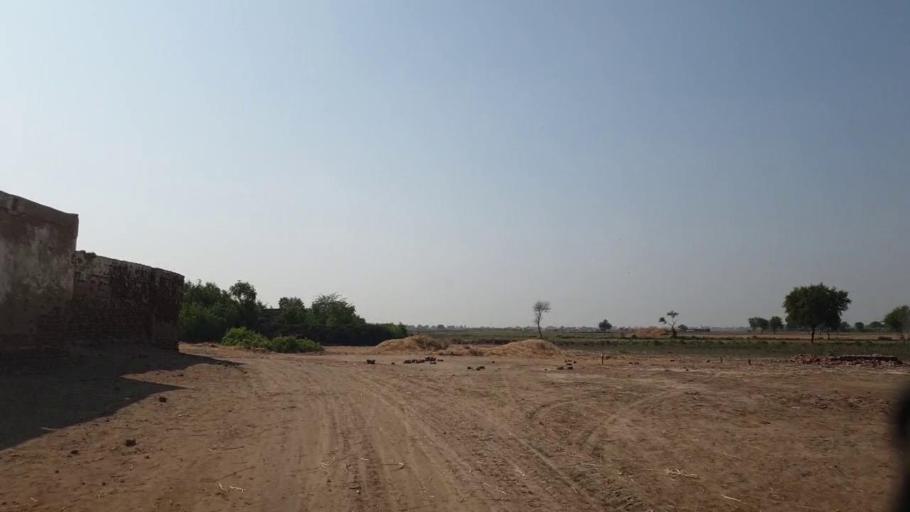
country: PK
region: Sindh
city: Tando Muhammad Khan
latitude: 25.0113
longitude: 68.4164
